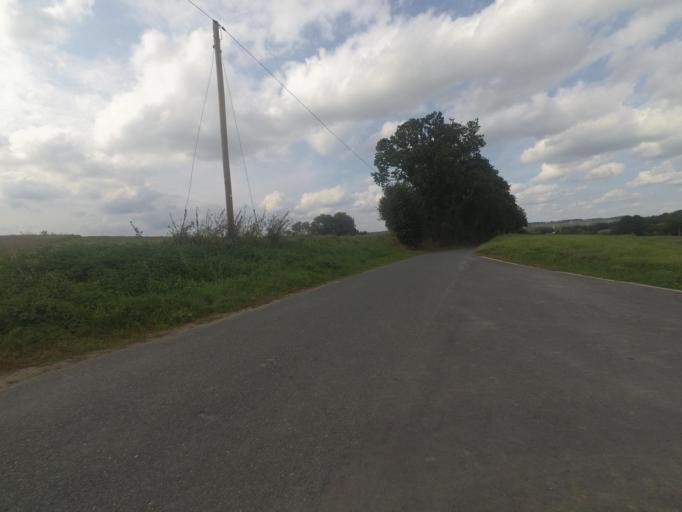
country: DE
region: North Rhine-Westphalia
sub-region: Regierungsbezirk Arnsberg
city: Holzwickede
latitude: 51.4505
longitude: 7.6545
